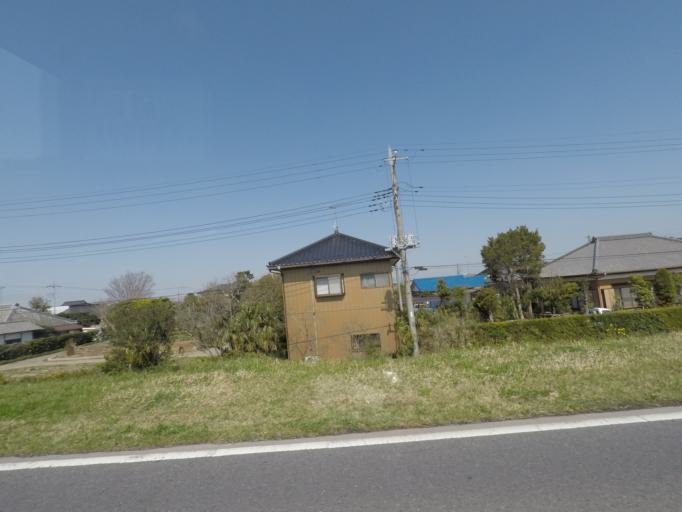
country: JP
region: Ibaraki
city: Edosaki
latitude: 35.8984
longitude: 140.3568
